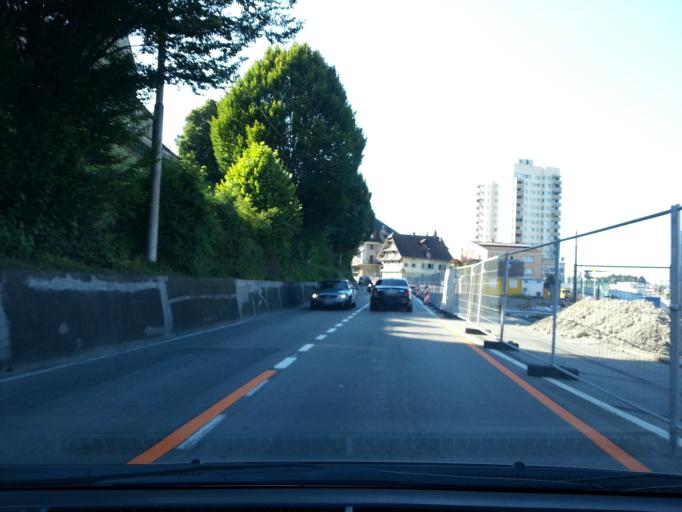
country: CH
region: Lucerne
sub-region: Hochdorf District
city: Emmen
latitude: 47.0642
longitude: 8.2840
